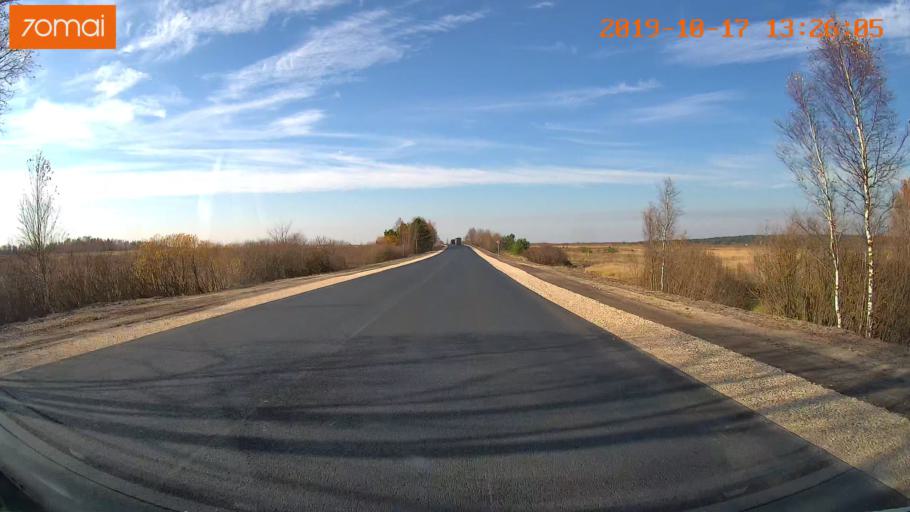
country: RU
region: Rjazan
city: Gus'-Zheleznyy
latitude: 55.1076
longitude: 40.9298
